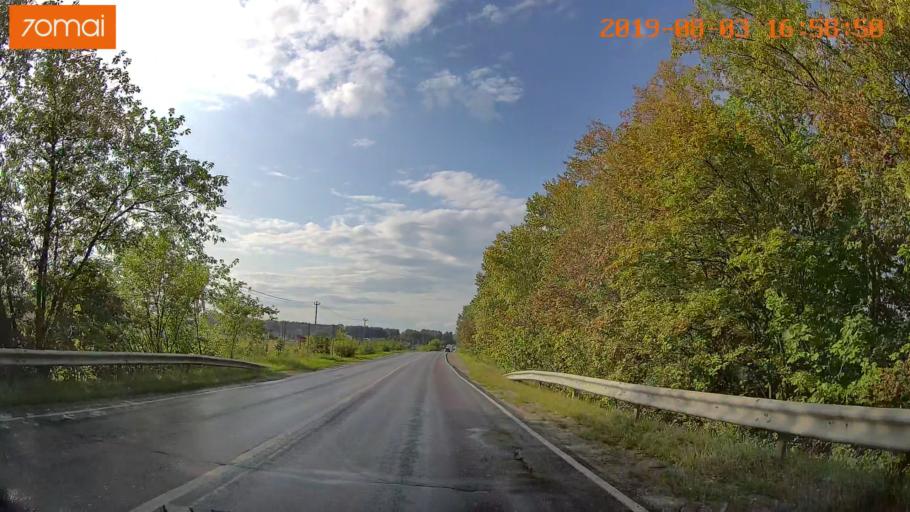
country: RU
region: Moskovskaya
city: Voskresensk
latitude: 55.3246
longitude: 38.6304
